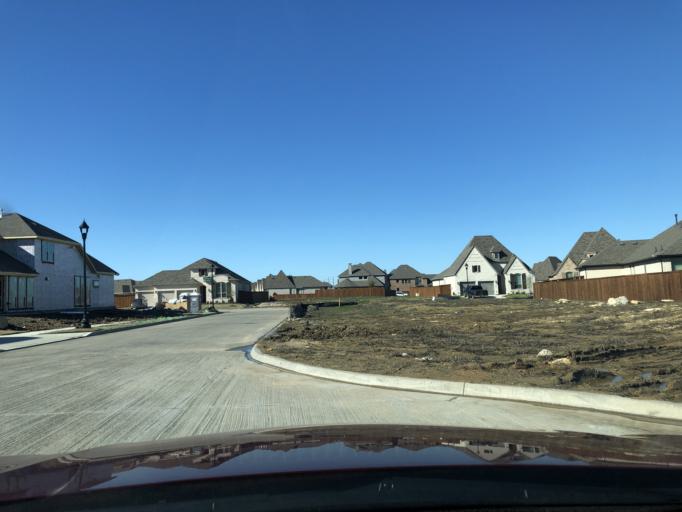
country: US
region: Texas
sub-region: Tarrant County
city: Haslet
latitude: 32.9472
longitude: -97.3935
